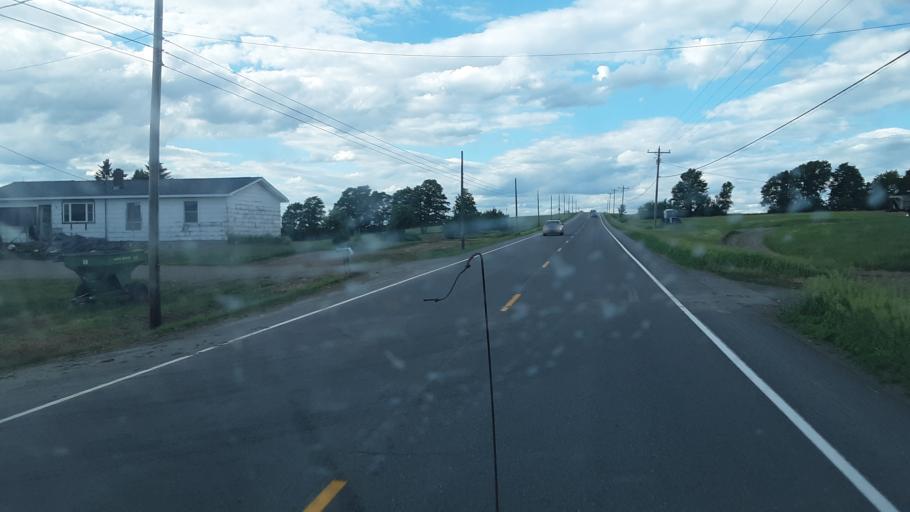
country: US
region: Maine
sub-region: Penobscot County
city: Patten
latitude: 45.9500
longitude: -68.4525
